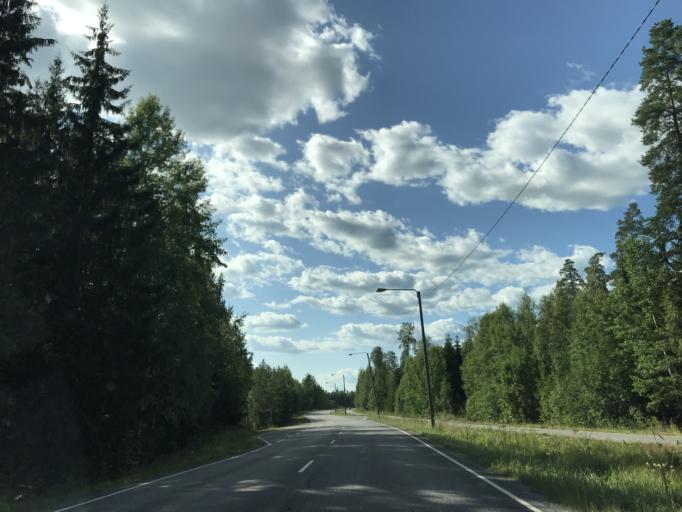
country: FI
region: Uusimaa
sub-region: Helsinki
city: Nurmijaervi
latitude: 60.4349
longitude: 24.8403
